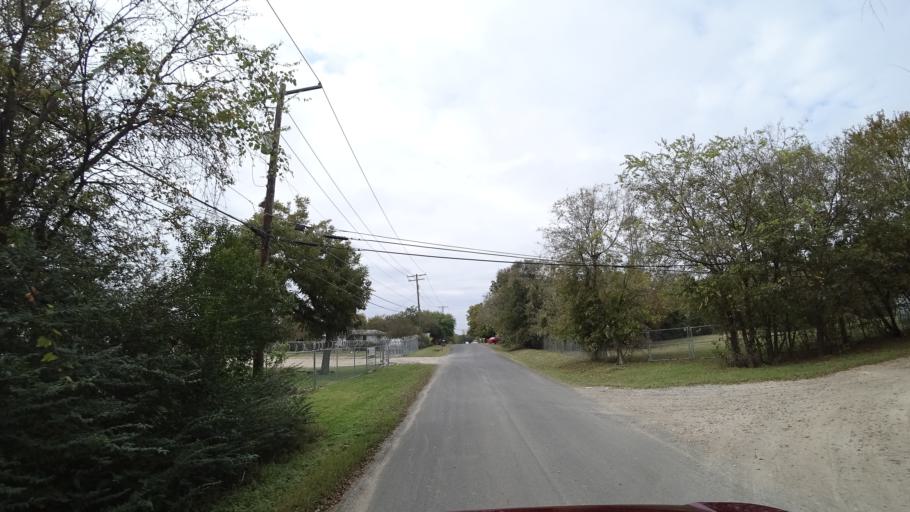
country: US
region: Texas
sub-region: Travis County
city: Wells Branch
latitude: 30.4344
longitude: -97.6903
